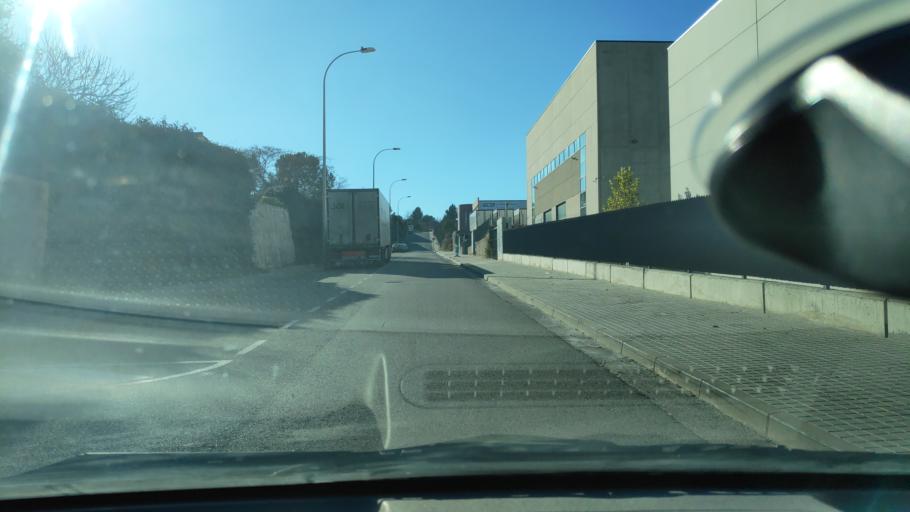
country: ES
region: Catalonia
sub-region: Provincia de Barcelona
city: Sant Quirze del Valles
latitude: 41.5243
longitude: 2.0926
